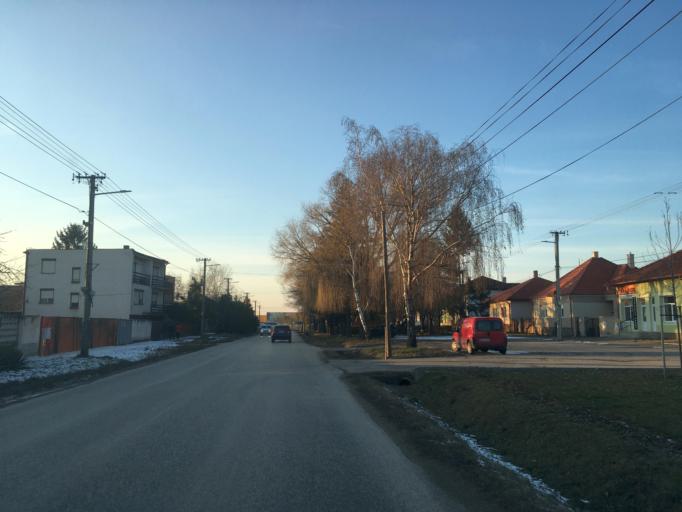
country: SK
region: Nitriansky
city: Svodin
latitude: 47.8505
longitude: 18.5124
